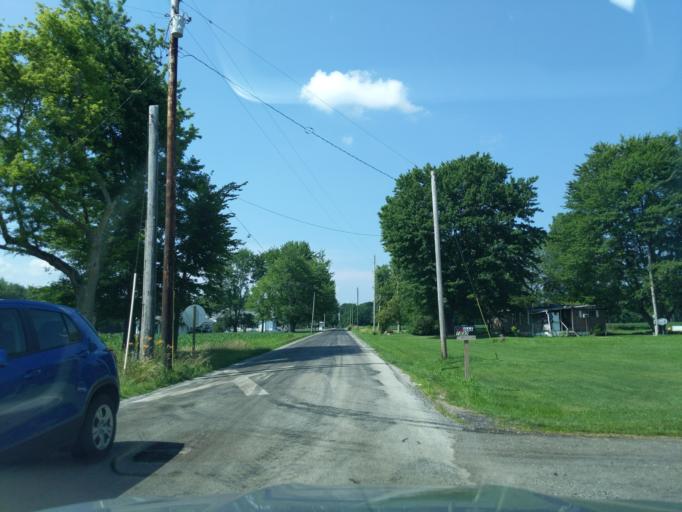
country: US
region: Indiana
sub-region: Ripley County
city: Osgood
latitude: 39.0902
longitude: -85.3466
